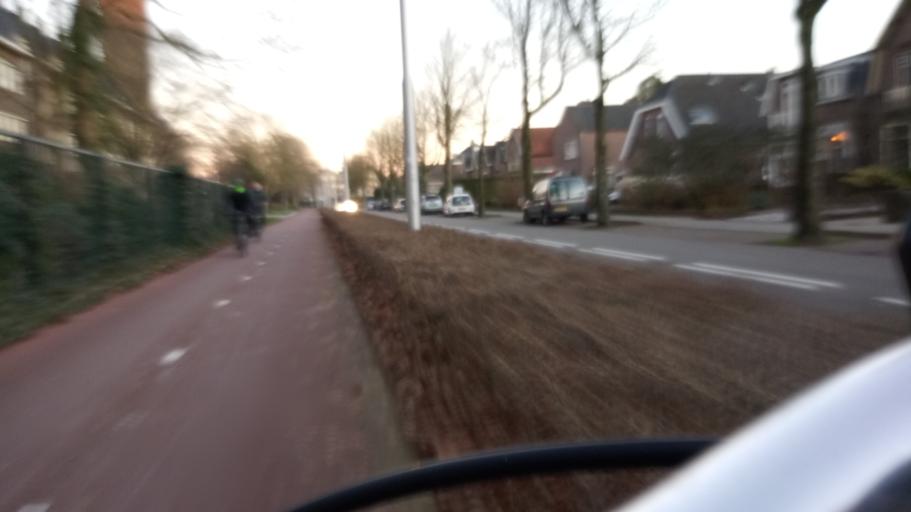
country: NL
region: Gelderland
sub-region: Gemeente Nijmegen
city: Nijmegen
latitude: 51.8165
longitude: 5.8634
